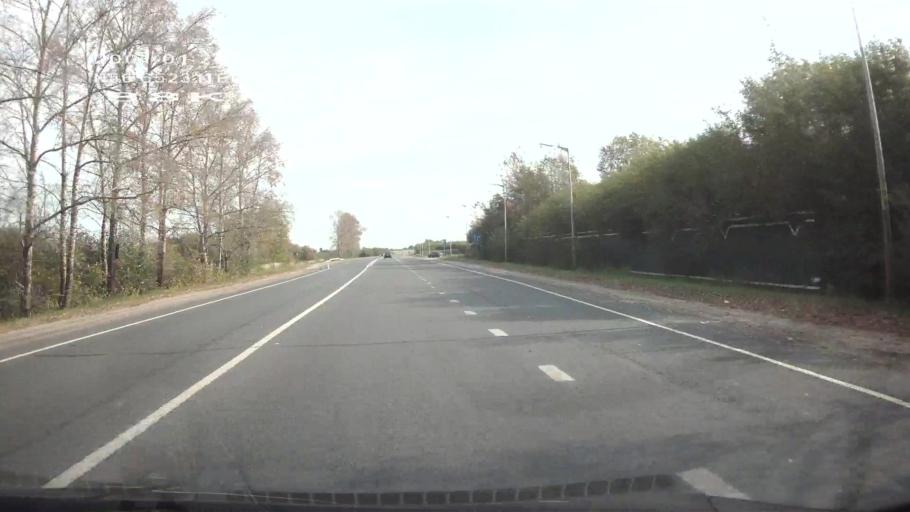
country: RU
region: Mariy-El
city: Yoshkar-Ola
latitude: 56.6523
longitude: 47.9511
